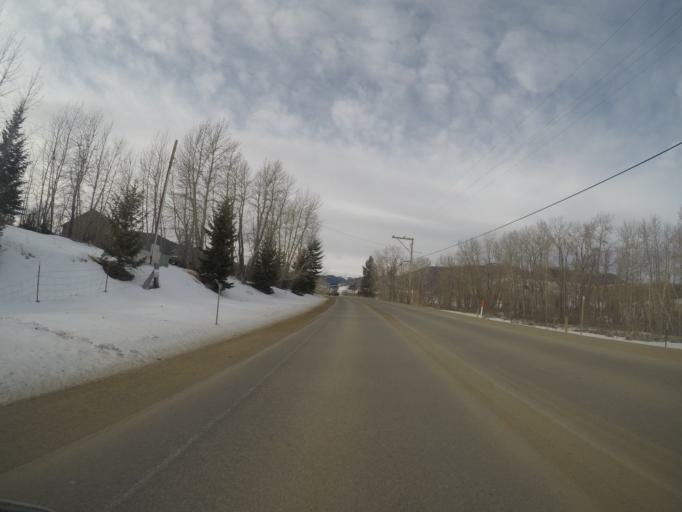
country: US
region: Montana
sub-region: Carbon County
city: Red Lodge
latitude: 45.1683
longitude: -109.2729
